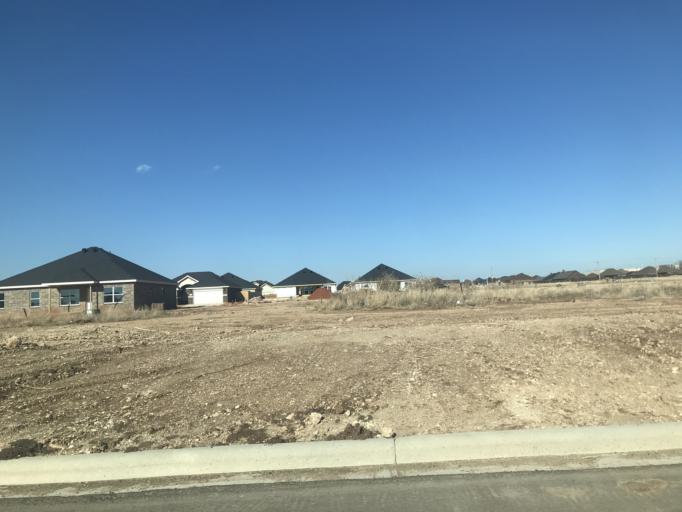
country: US
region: Texas
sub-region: Taylor County
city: Potosi
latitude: 32.3695
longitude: -99.7192
